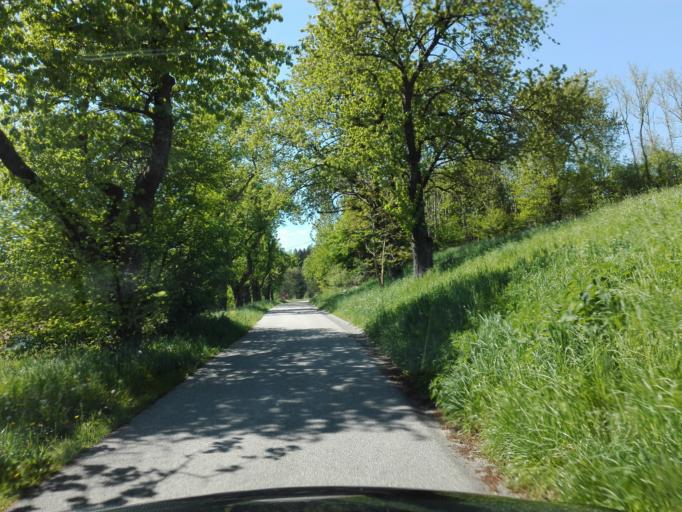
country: AT
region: Upper Austria
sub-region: Politischer Bezirk Urfahr-Umgebung
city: Feldkirchen an der Donau
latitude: 48.3438
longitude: 13.9673
